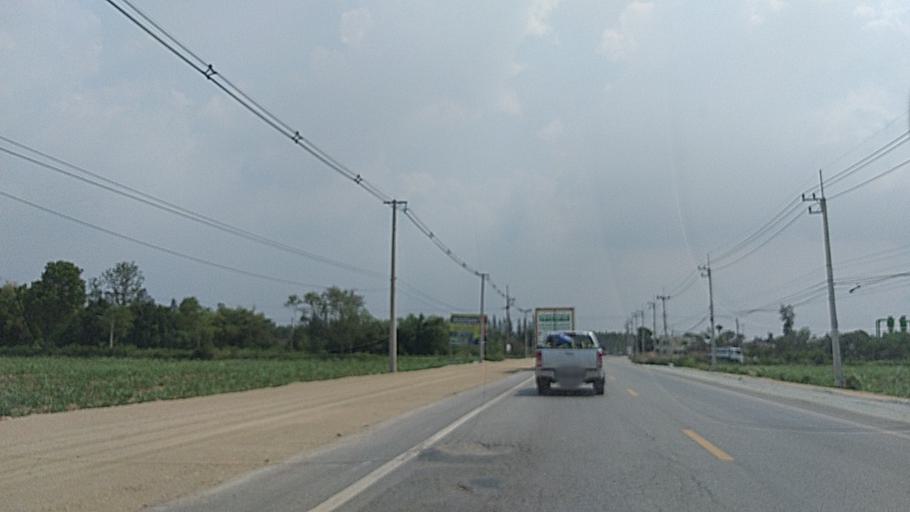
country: TH
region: Chon Buri
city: Phanat Nikhom
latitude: 13.3653
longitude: 101.1962
